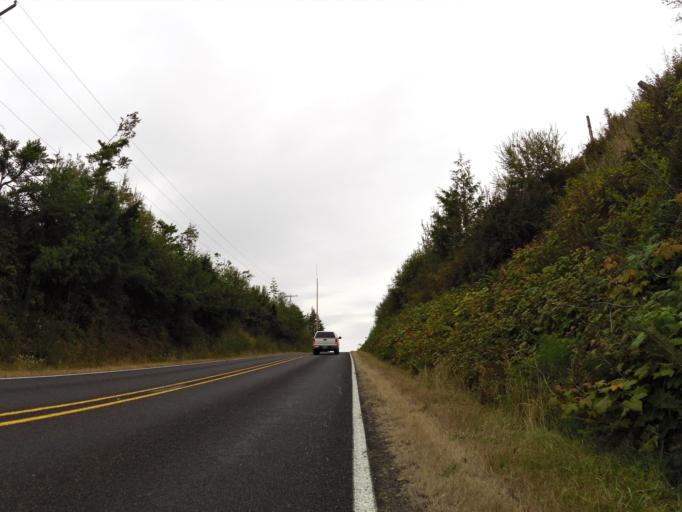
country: US
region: Washington
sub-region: Jefferson County
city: Port Ludlow
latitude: 47.9114
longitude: -122.6690
